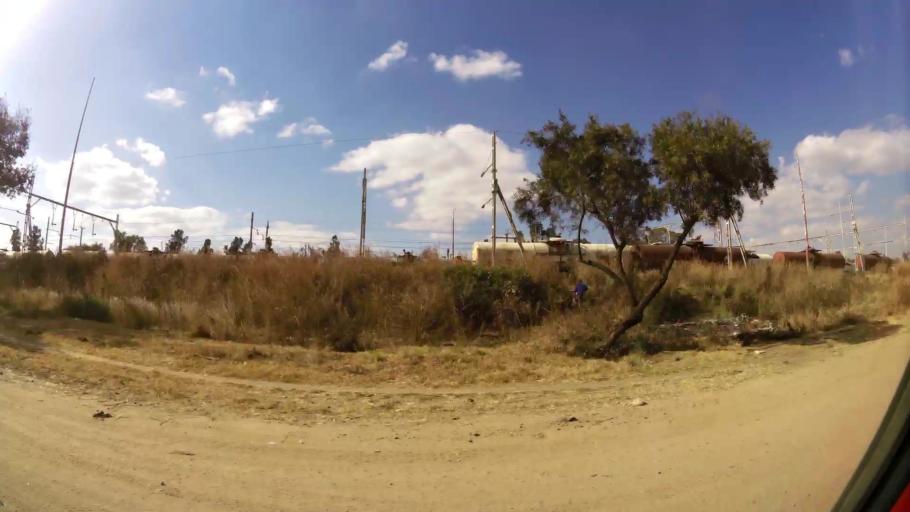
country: ZA
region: Gauteng
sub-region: Ekurhuleni Metropolitan Municipality
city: Tembisa
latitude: -25.9626
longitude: 28.2327
